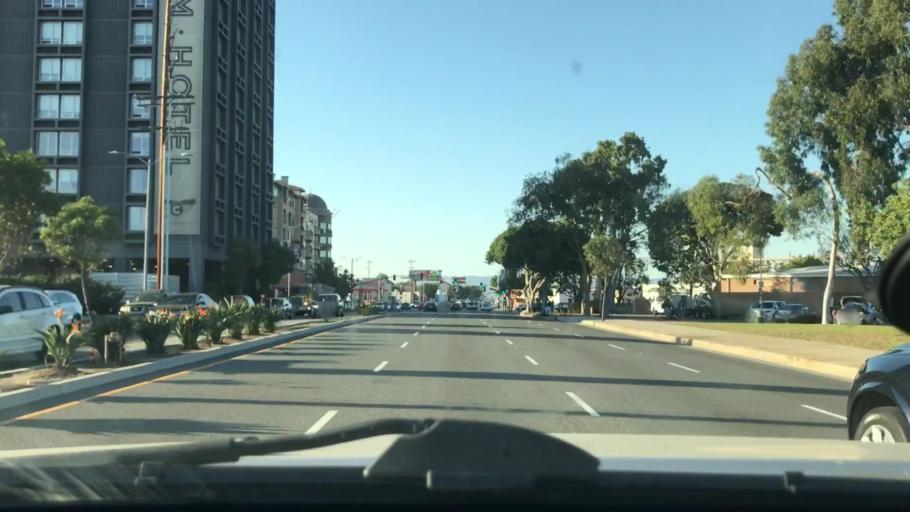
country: US
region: California
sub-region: Los Angeles County
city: El Segundo
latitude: 33.9583
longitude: -118.4177
